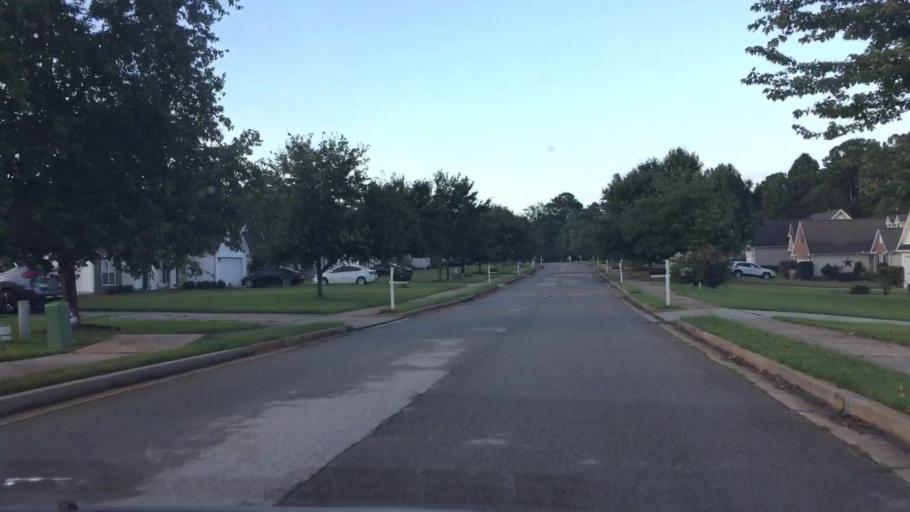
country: US
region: Georgia
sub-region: Henry County
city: Hampton
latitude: 33.4115
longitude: -84.2853
